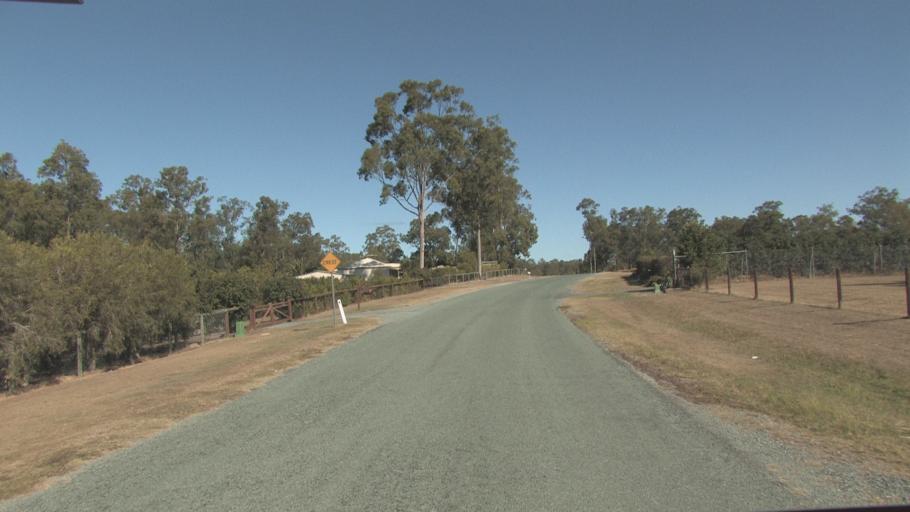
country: AU
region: Queensland
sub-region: Logan
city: Cedar Vale
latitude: -27.8635
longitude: 153.0340
